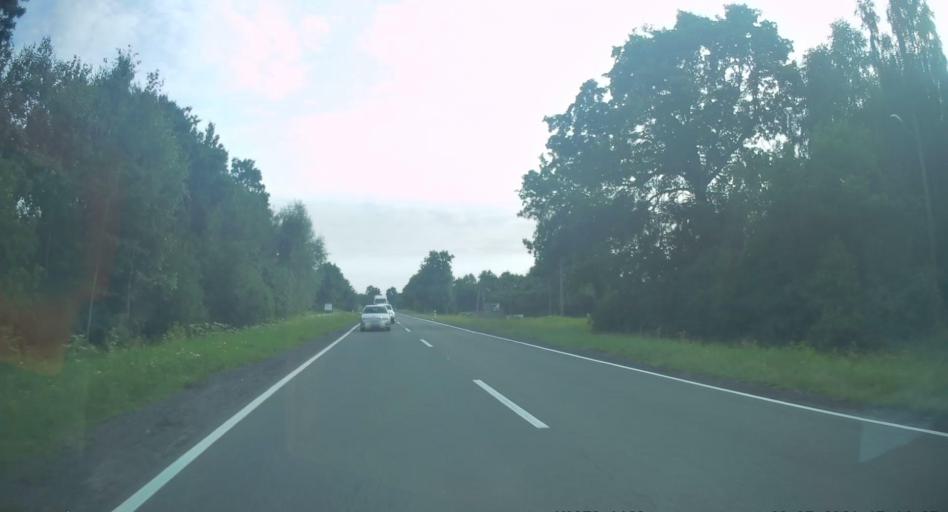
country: PL
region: Silesian Voivodeship
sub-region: Powiat czestochowski
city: Klomnice
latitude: 50.9332
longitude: 19.3824
